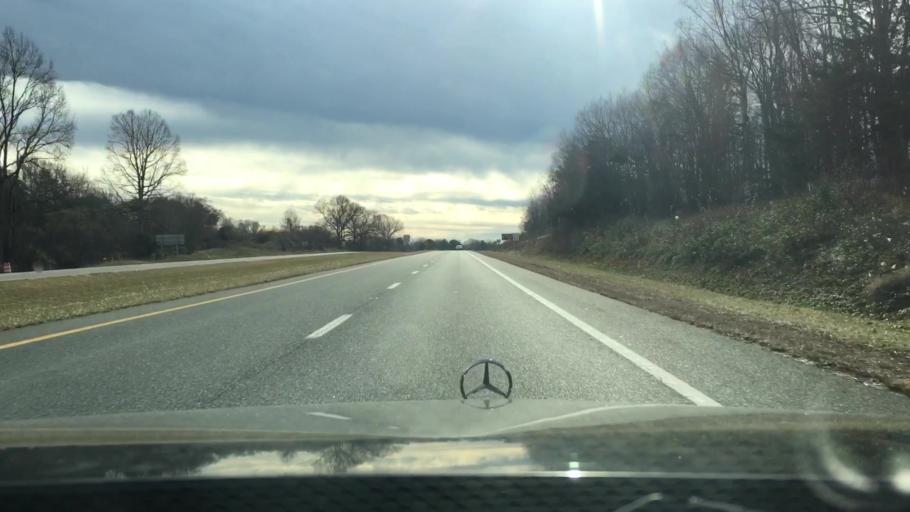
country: US
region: Virginia
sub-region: Pittsylvania County
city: Motley
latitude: 37.0690
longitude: -79.3400
